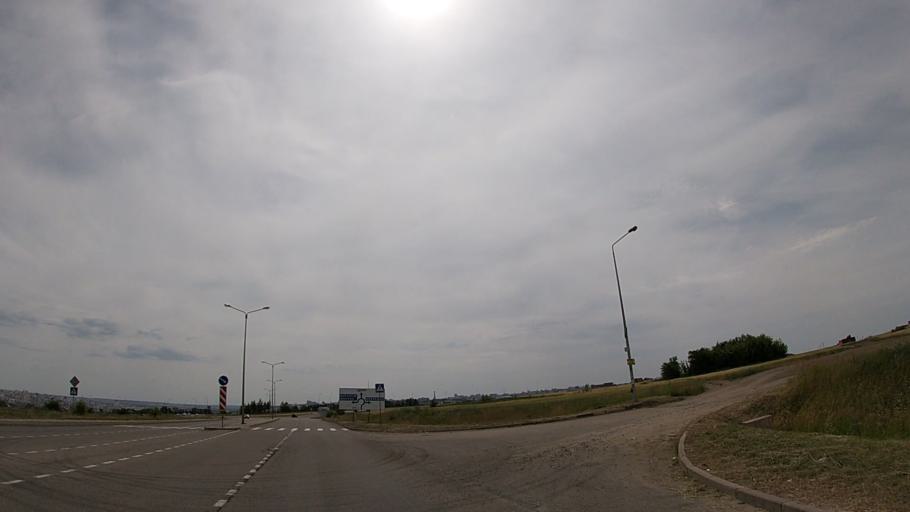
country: RU
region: Belgorod
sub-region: Belgorodskiy Rayon
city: Belgorod
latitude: 50.5941
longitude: 36.5267
